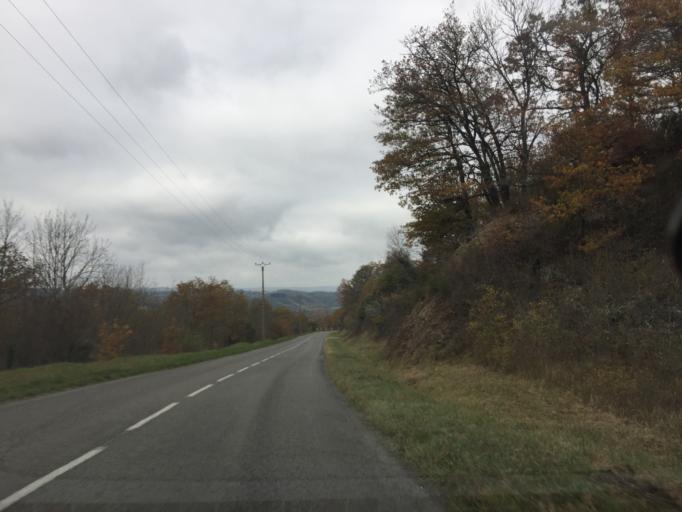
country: FR
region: Limousin
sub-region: Departement de la Creuse
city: Ahun
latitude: 46.0792
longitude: 2.1041
